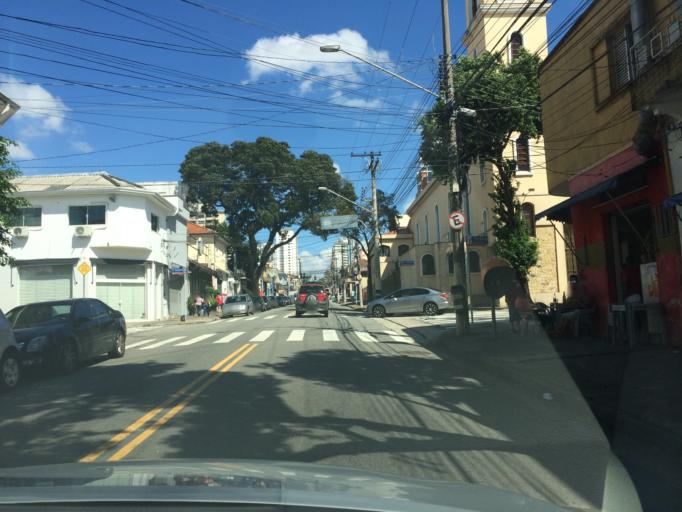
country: BR
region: Sao Paulo
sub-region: Sao Caetano Do Sul
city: Sao Caetano do Sul
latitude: -23.5454
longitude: -46.5558
